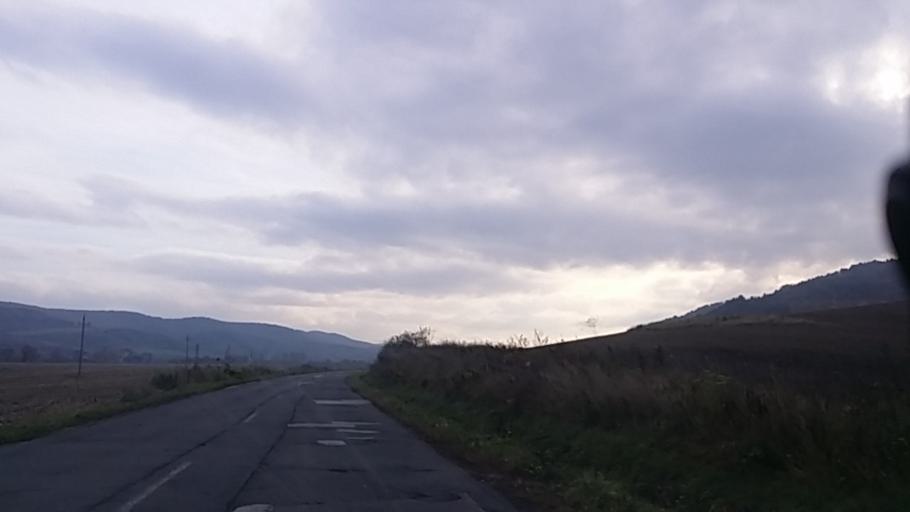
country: HU
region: Borsod-Abauj-Zemplen
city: Sajokaza
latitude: 48.2633
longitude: 20.5410
